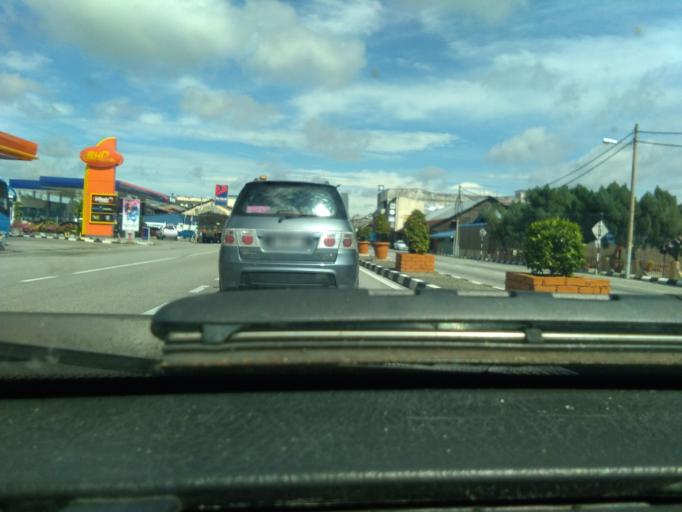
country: MY
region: Perak
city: Bagan Serai
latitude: 5.0090
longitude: 100.5383
